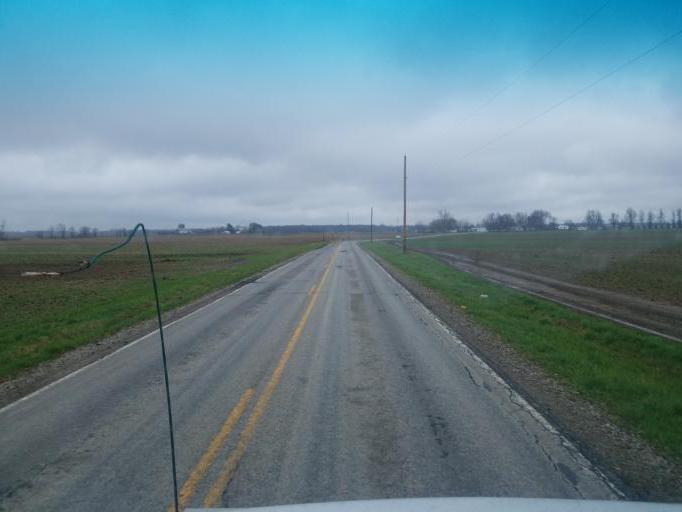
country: US
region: Ohio
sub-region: Huron County
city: Plymouth
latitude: 40.9411
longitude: -82.6435
